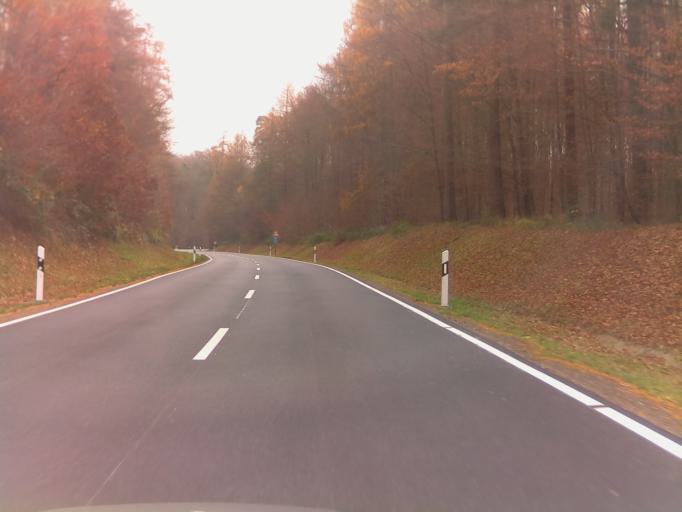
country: DE
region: Baden-Wuerttemberg
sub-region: Karlsruhe Region
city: Neunkirchen
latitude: 49.3978
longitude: 8.9952
